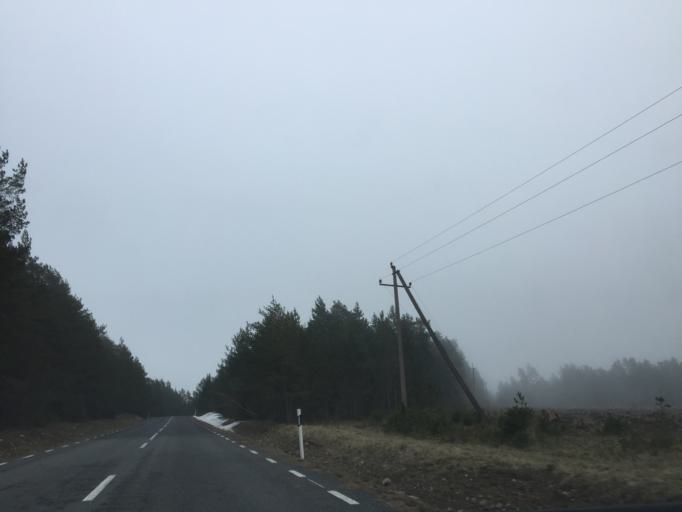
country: EE
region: Saare
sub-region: Kuressaare linn
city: Kuressaare
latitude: 58.4659
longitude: 22.0420
